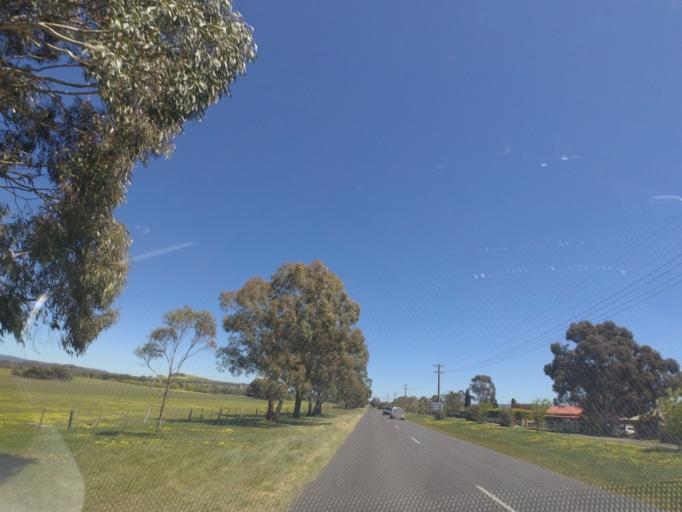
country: AU
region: Victoria
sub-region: Hume
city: Sunbury
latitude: -37.2792
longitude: 144.7202
